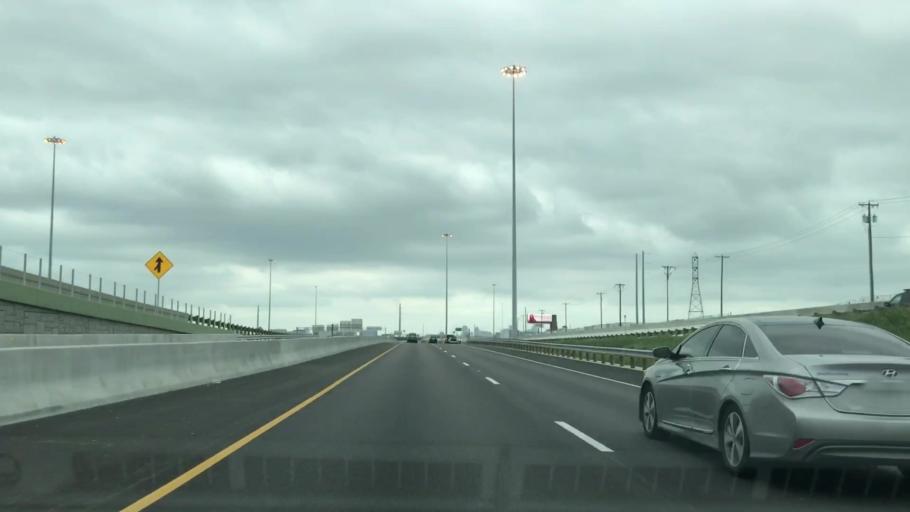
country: US
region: Texas
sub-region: Dallas County
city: Irving
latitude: 32.8359
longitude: -96.9019
